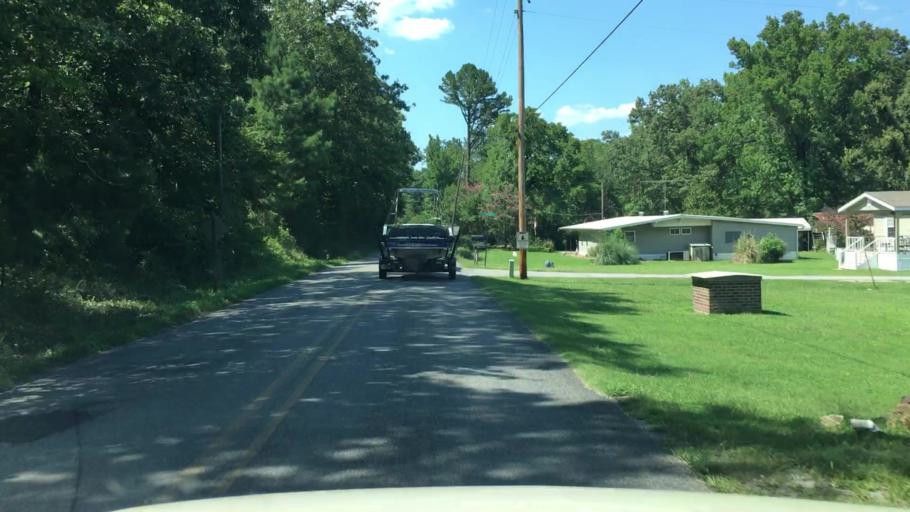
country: US
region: Arkansas
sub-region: Garland County
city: Piney
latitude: 34.5286
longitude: -93.3359
